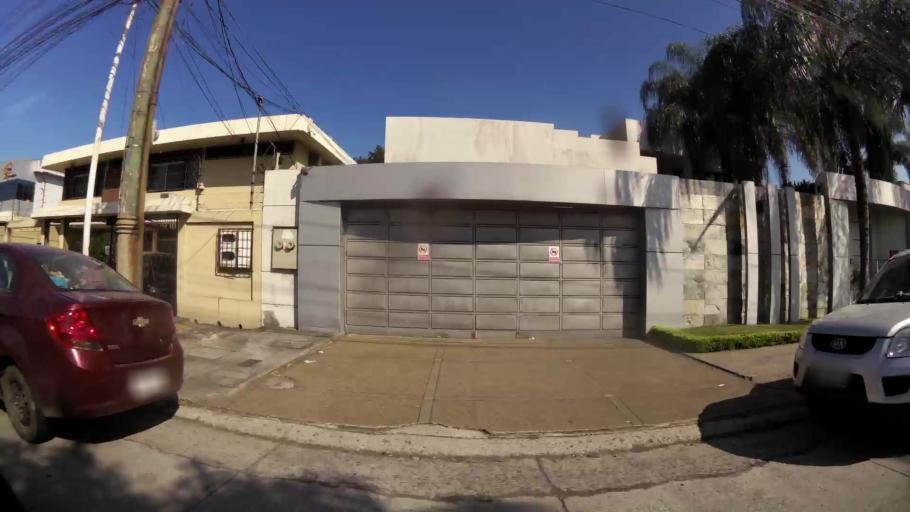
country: EC
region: Guayas
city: Guayaquil
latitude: -2.1692
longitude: -79.9053
